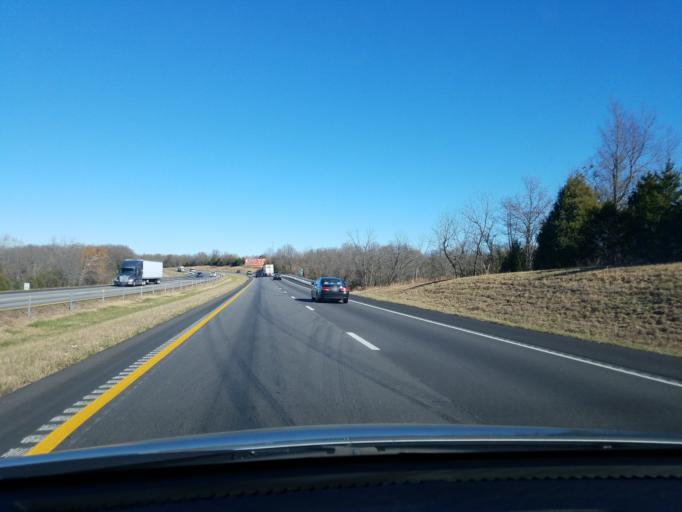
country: US
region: Missouri
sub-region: Webster County
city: Marshfield
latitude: 37.3563
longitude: -92.9137
